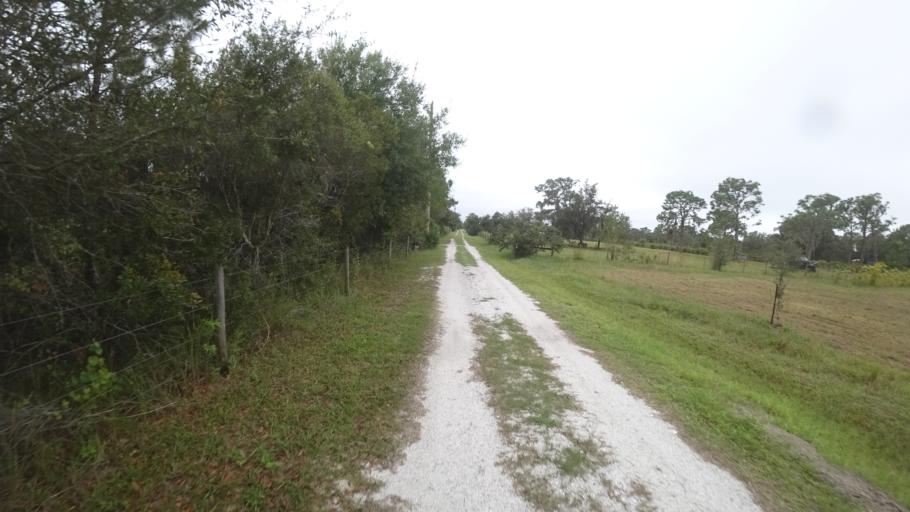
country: US
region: Florida
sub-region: Sarasota County
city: Warm Mineral Springs
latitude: 27.2770
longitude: -82.1327
